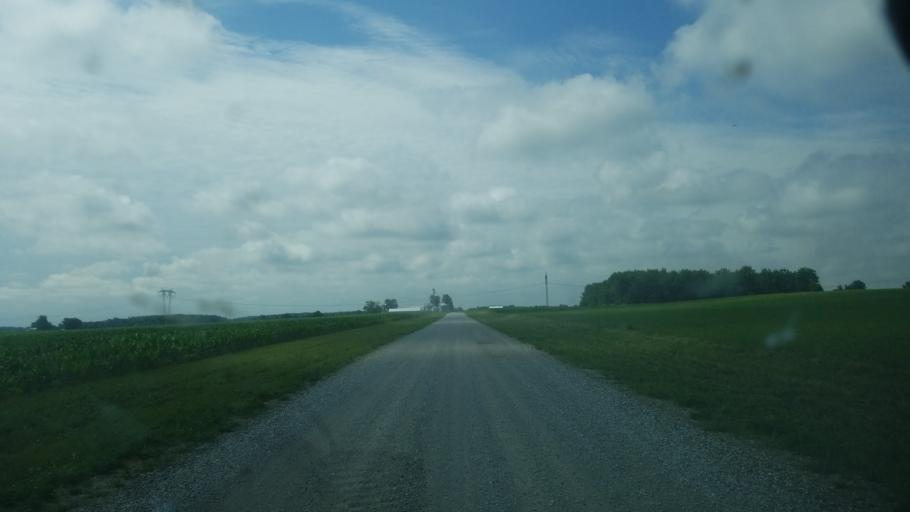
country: US
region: Ohio
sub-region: Licking County
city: Johnstown
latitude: 40.2165
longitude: -82.7393
